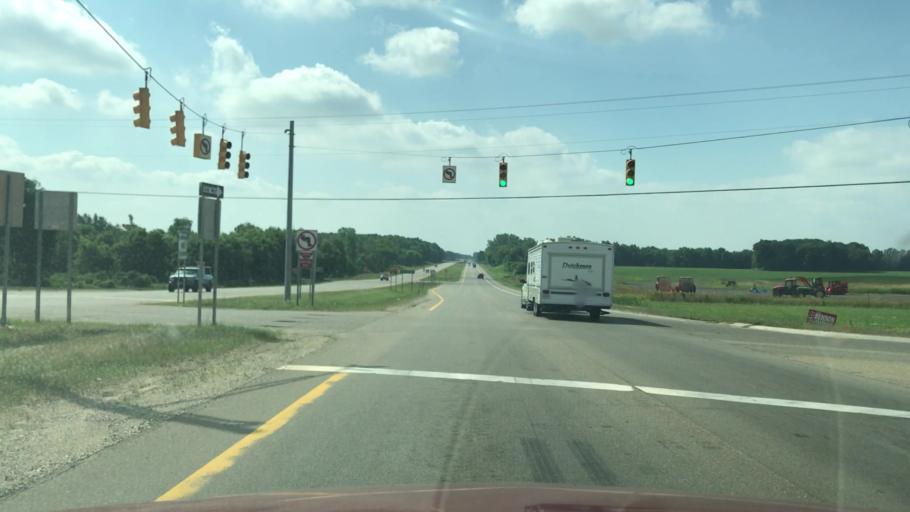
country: US
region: Michigan
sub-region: Kent County
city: Sparta
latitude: 43.1172
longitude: -85.7059
